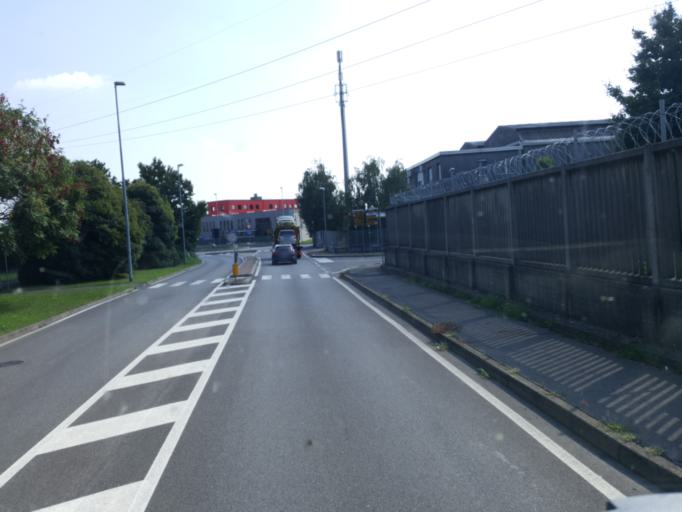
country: IT
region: Lombardy
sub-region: Citta metropolitana di Milano
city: Settimo Milanese
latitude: 45.4670
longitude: 9.0614
